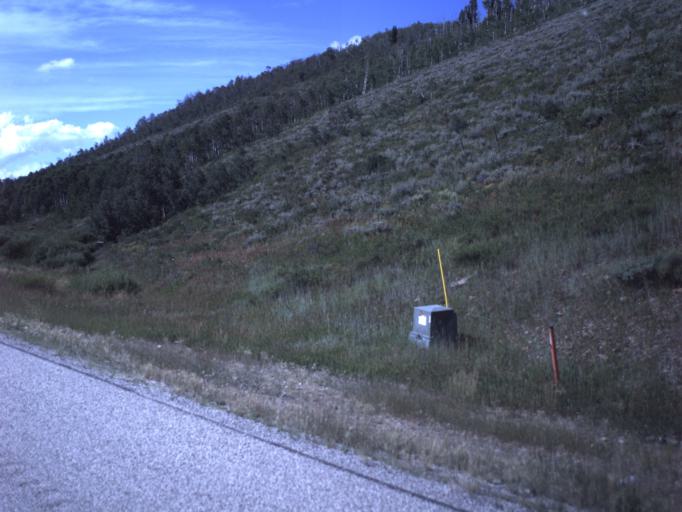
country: US
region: Utah
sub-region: Wasatch County
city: Heber
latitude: 40.2893
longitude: -111.2467
